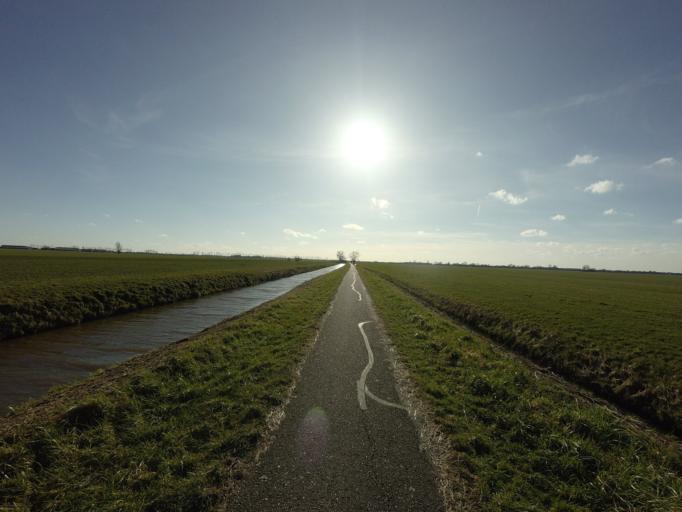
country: NL
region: Utrecht
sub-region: Gemeente Montfoort
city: Montfoort
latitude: 52.0486
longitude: 4.9881
